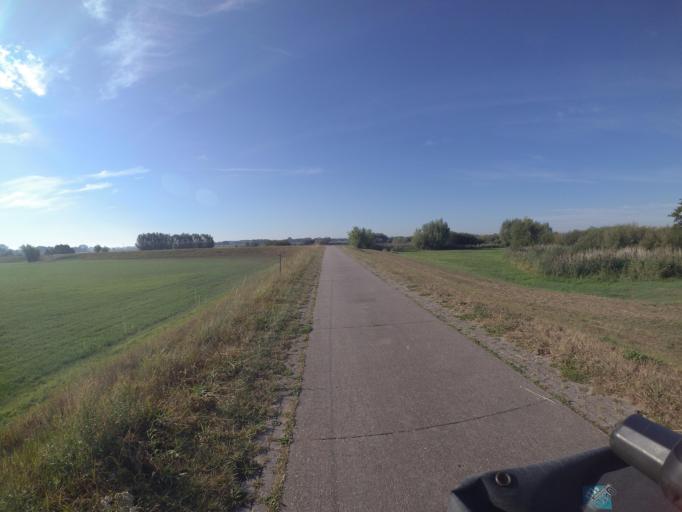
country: NL
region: Overijssel
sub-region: Gemeente Zwartewaterland
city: Hasselt
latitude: 52.5618
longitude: 6.1097
